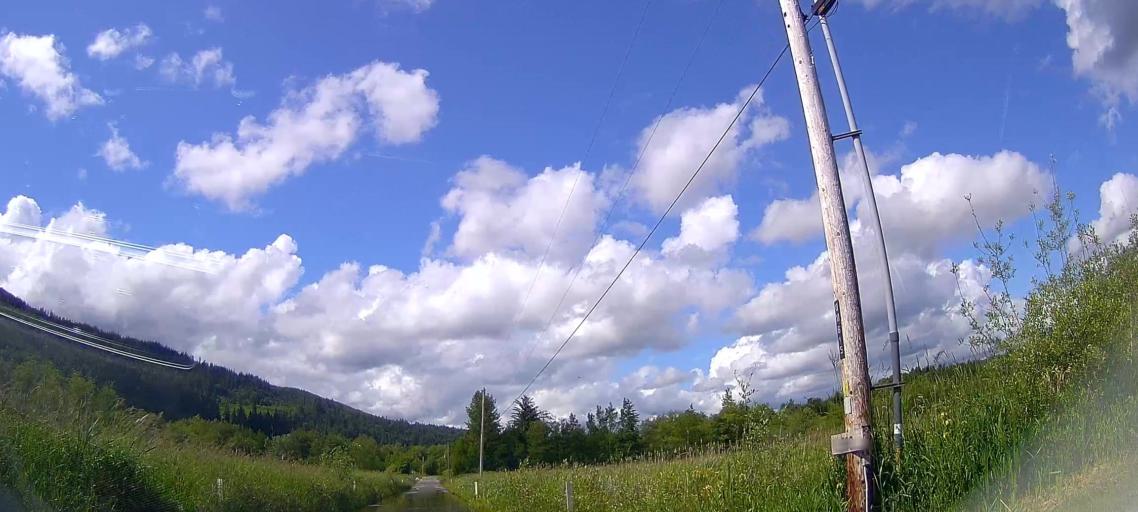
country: US
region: Washington
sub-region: Whatcom County
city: Sudden Valley
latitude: 48.6712
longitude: -122.1954
